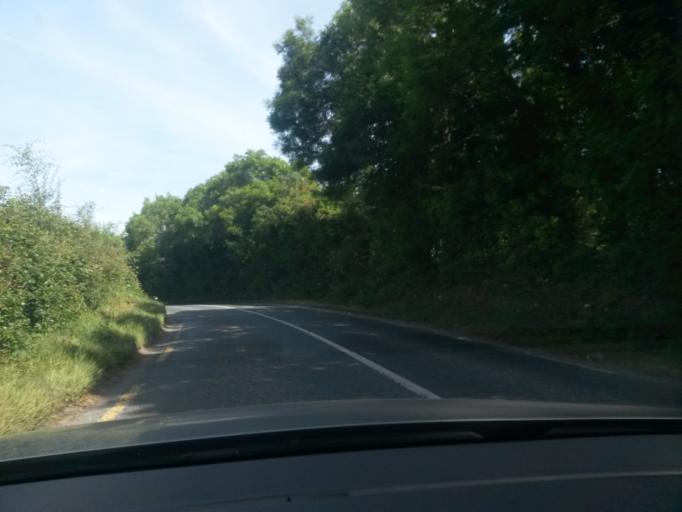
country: IE
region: Leinster
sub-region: Kildare
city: Eadestown
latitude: 53.1988
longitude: -6.6135
